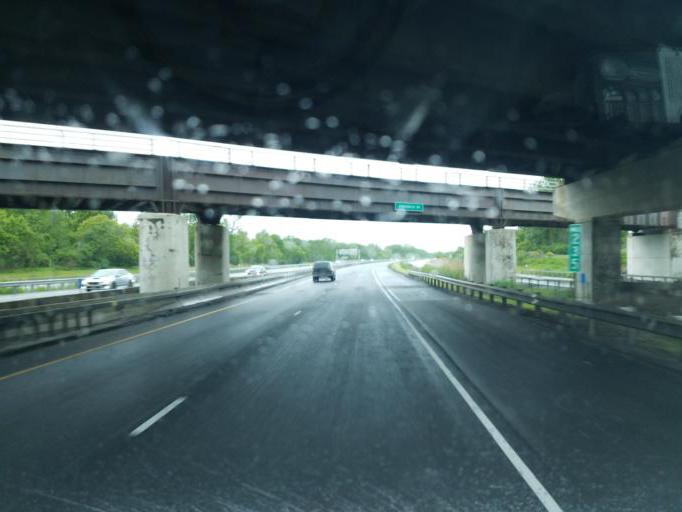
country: US
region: New York
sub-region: Oneida County
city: Utica
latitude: 43.1254
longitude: -75.2432
